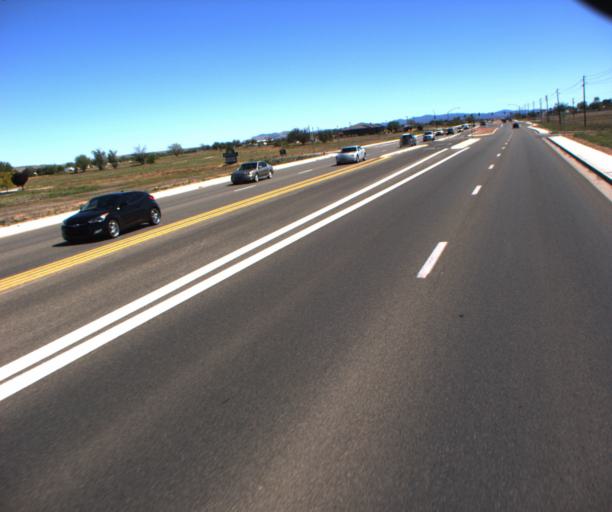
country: US
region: Arizona
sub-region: Yavapai County
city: Chino Valley
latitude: 34.7417
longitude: -112.4546
